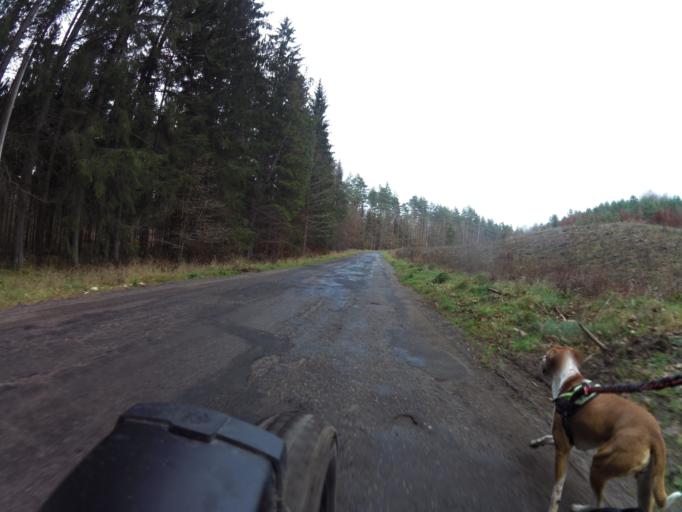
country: PL
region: West Pomeranian Voivodeship
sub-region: Powiat koszalinski
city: Polanow
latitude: 54.0722
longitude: 16.6517
